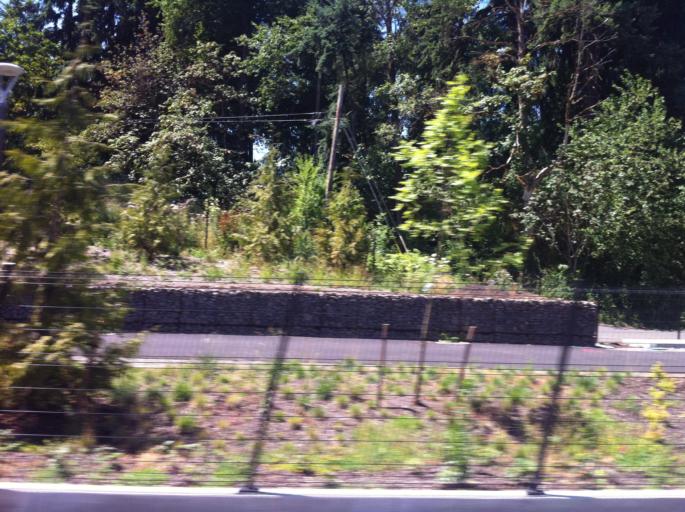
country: US
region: Oregon
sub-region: Clackamas County
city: Milwaukie
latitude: 45.4344
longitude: -122.6364
